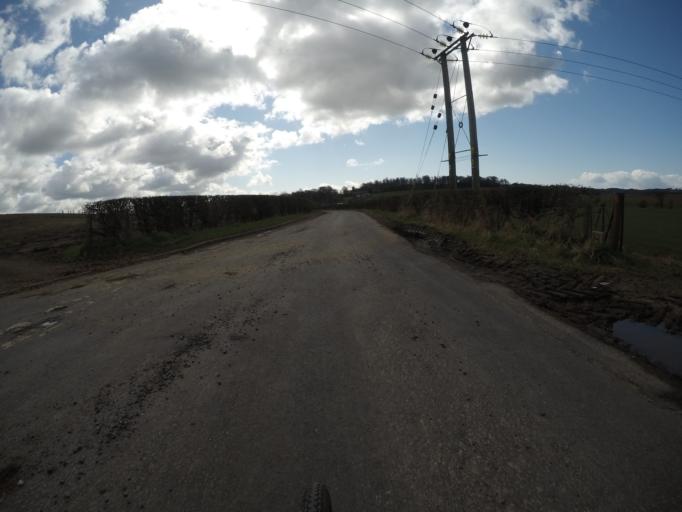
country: GB
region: Scotland
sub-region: South Ayrshire
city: Dundonald
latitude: 55.5887
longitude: -4.5776
